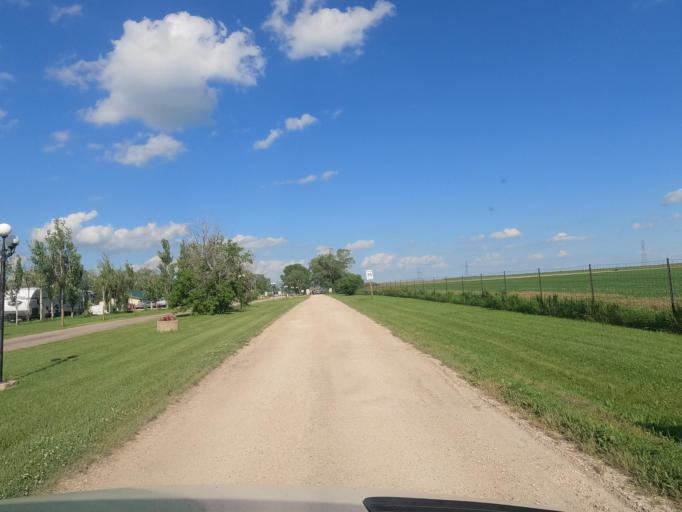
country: CA
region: Manitoba
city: Winnipeg
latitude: 49.8267
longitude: -96.9805
